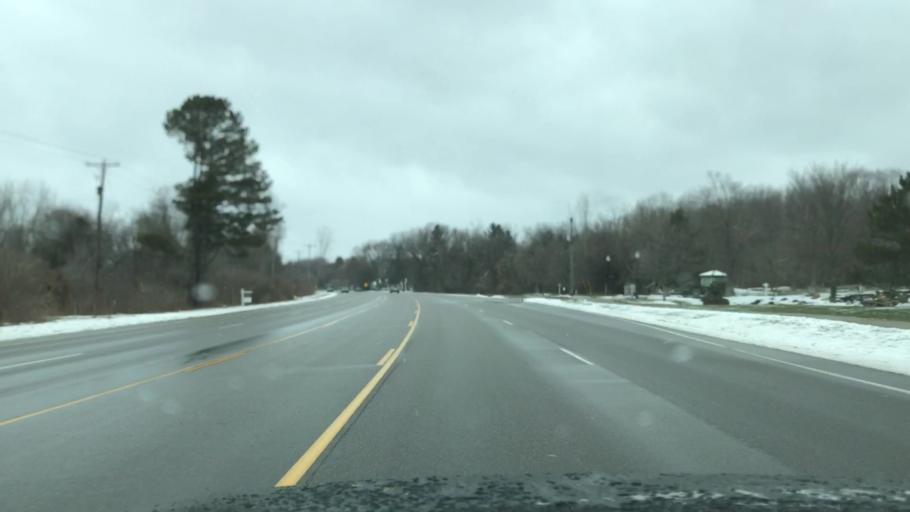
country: US
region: Michigan
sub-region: Kent County
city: Forest Hills
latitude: 42.9220
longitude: -85.5062
